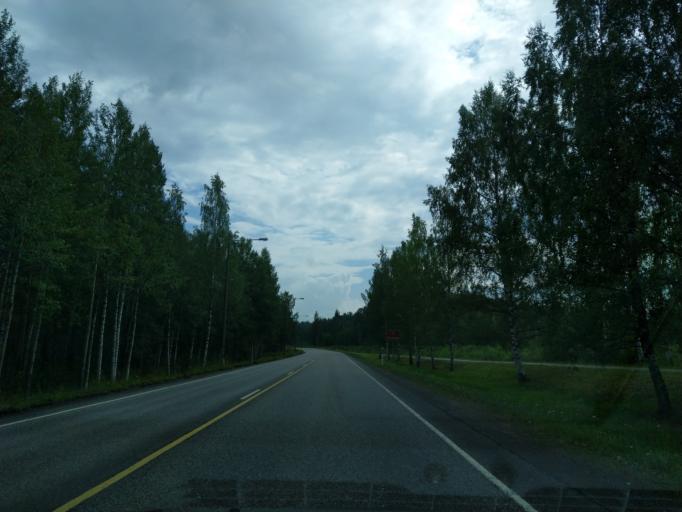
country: FI
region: South Karelia
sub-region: Imatra
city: Parikkala
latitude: 61.5968
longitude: 29.4839
